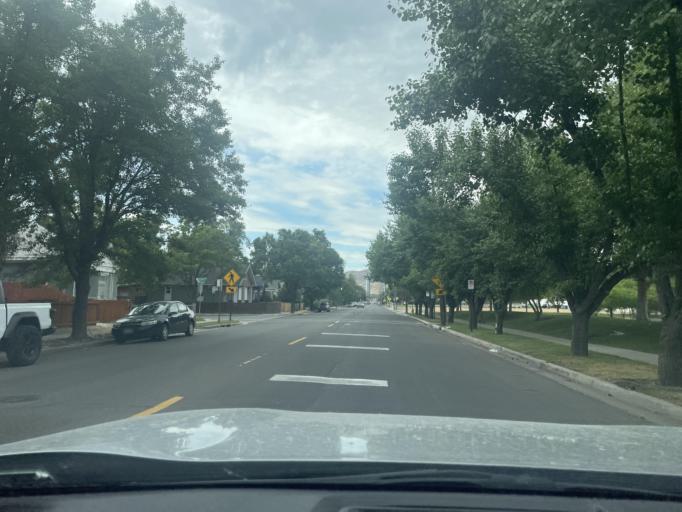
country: US
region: Utah
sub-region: Salt Lake County
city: Salt Lake City
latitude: 40.7424
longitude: -111.8939
